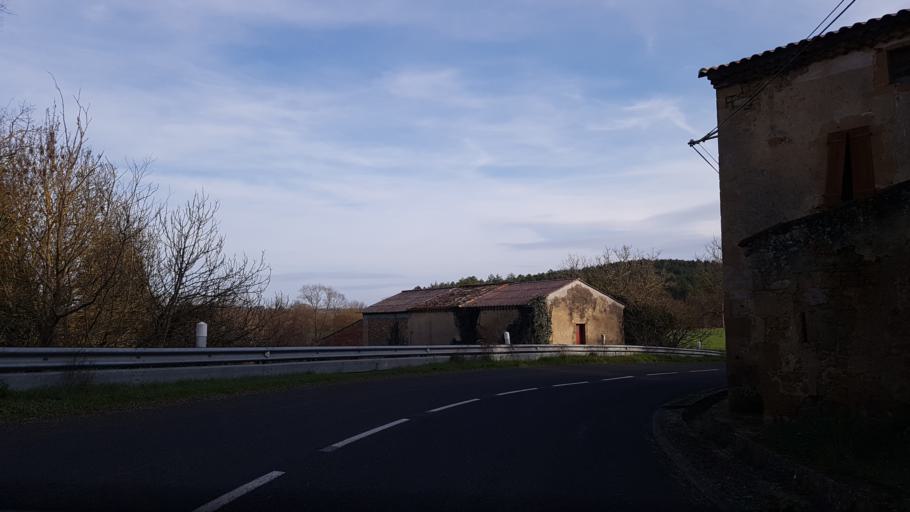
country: FR
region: Midi-Pyrenees
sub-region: Departement de l'Ariege
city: Mirepoix
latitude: 43.1776
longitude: 1.9147
